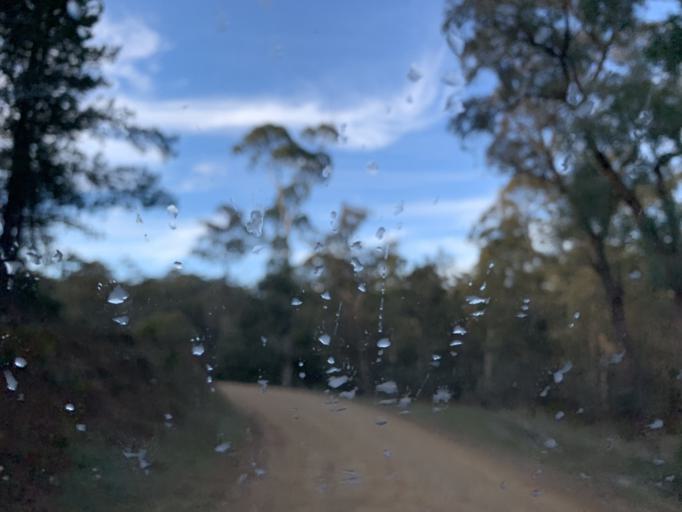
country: AU
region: Victoria
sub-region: Mansfield
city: Mansfield
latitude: -36.9257
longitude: 146.0987
